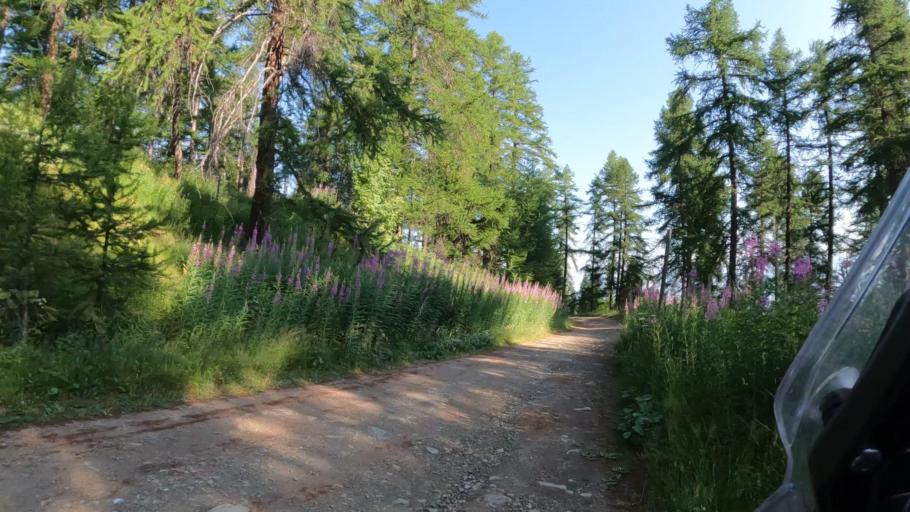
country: FR
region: Provence-Alpes-Cote d'Azur
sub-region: Departement des Hautes-Alpes
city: Guillestre
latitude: 44.6206
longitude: 6.6420
